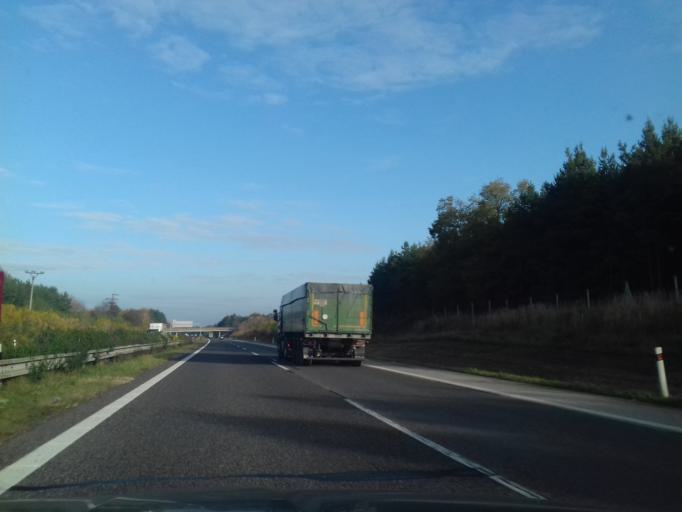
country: SK
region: Bratislavsky
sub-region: Okres Malacky
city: Malacky
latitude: 48.4382
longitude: 17.0432
